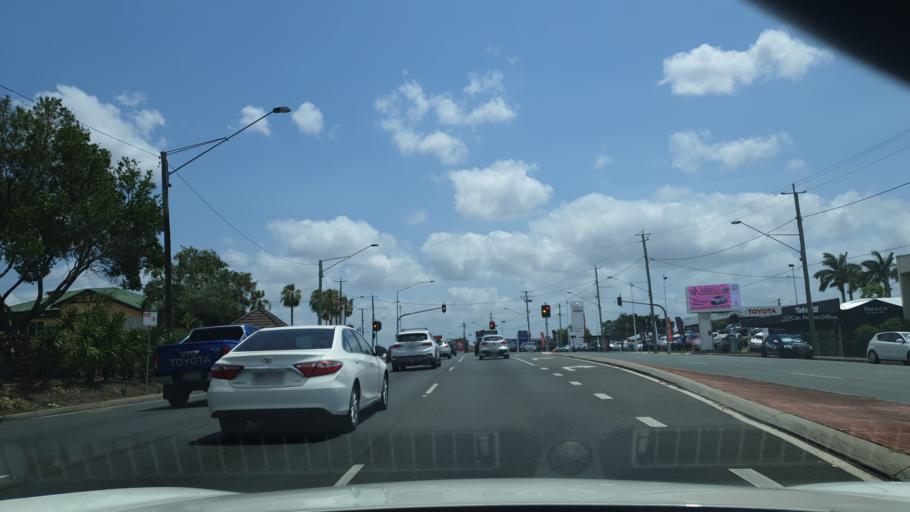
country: AU
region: Queensland
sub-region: Brisbane
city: Wavell Heights
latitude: -27.4007
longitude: 153.0314
